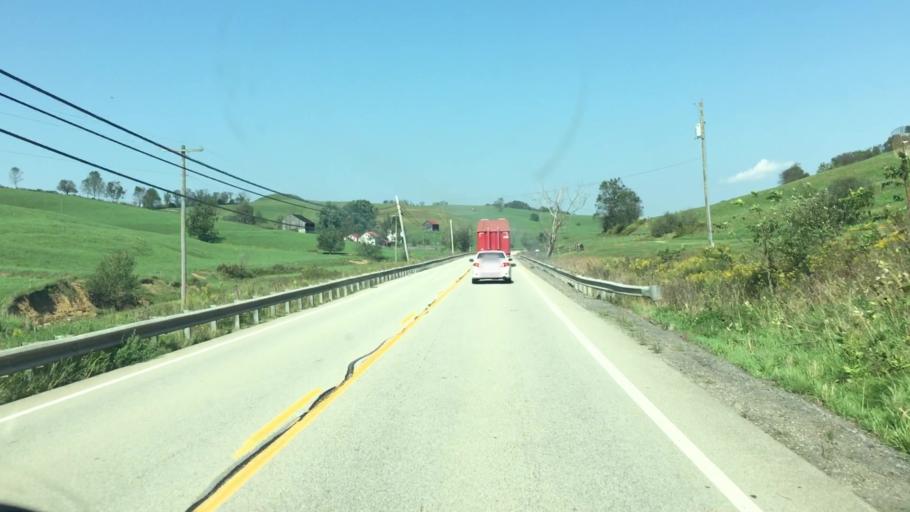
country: US
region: Pennsylvania
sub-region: Washington County
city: Washington
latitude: 40.0576
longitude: -80.2979
